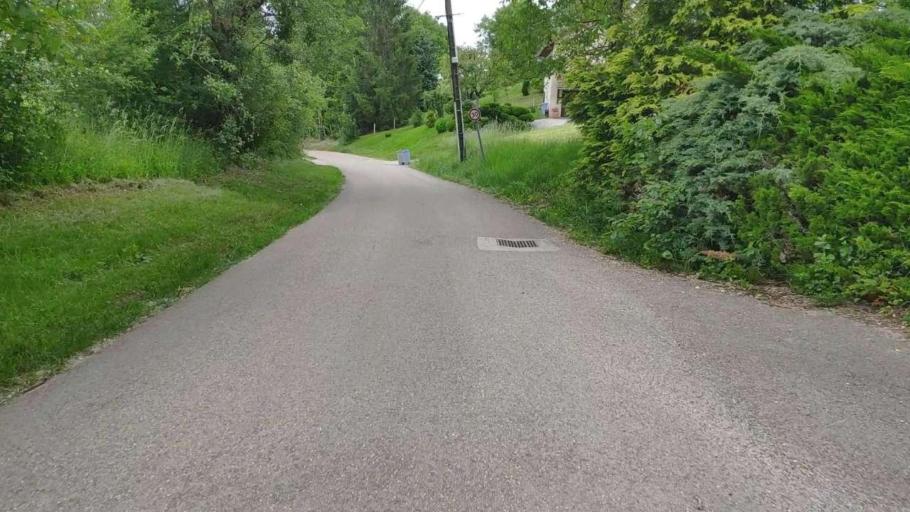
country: FR
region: Franche-Comte
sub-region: Departement du Jura
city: Montmorot
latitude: 46.7528
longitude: 5.5625
